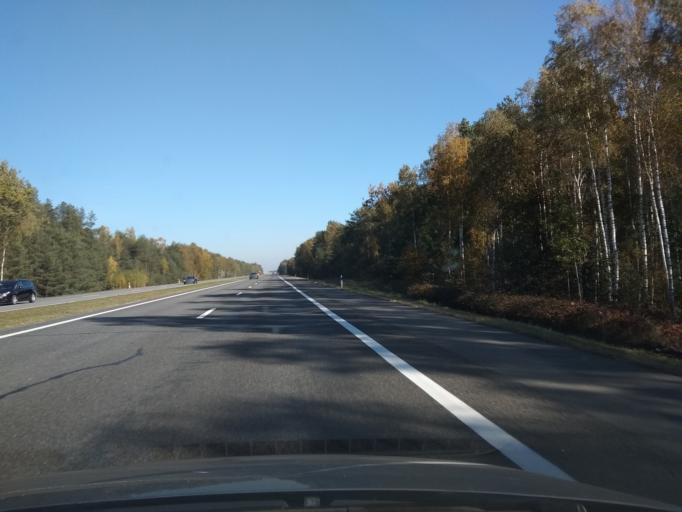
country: BY
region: Brest
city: Antopal'
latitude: 52.3741
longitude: 24.7489
